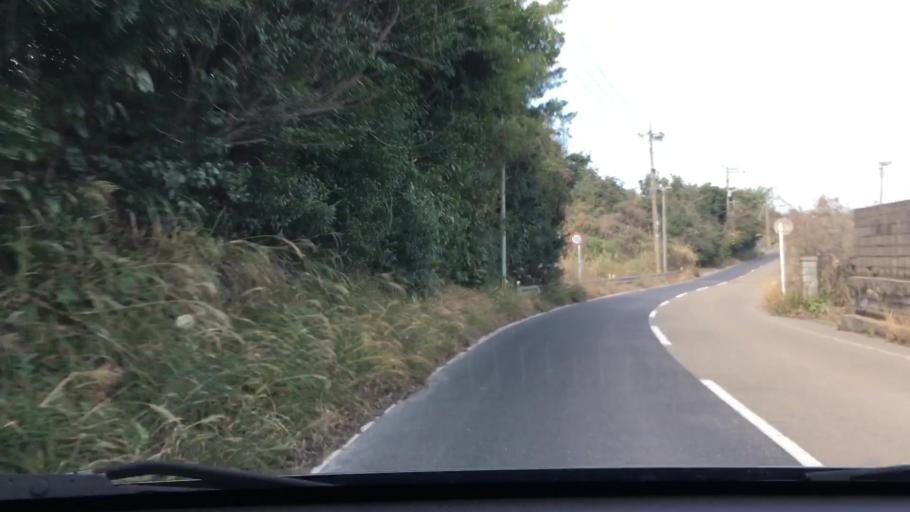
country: JP
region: Kagoshima
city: Hamanoichi
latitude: 31.6161
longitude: 130.7003
